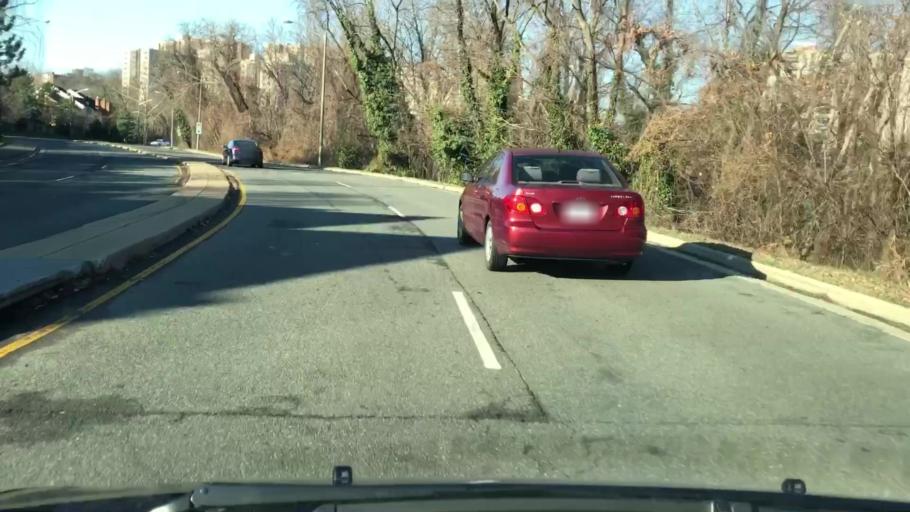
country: US
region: Virginia
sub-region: Fairfax County
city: Belle Haven
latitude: 38.7898
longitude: -77.0610
